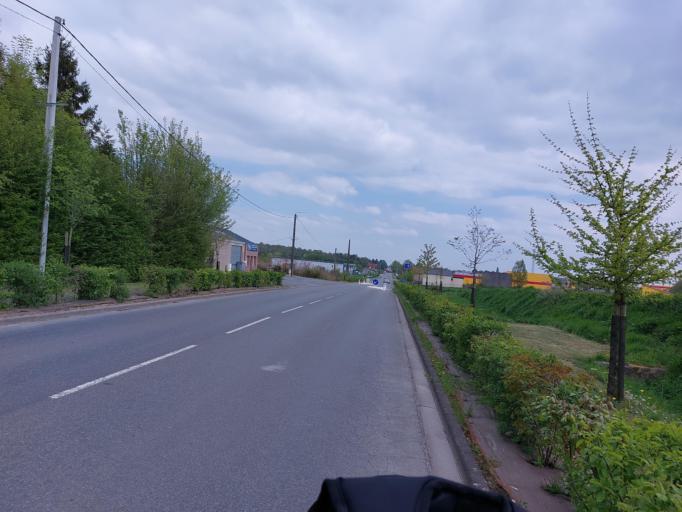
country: FR
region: Nord-Pas-de-Calais
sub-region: Departement du Nord
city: La Longueville
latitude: 50.2851
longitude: 3.8693
